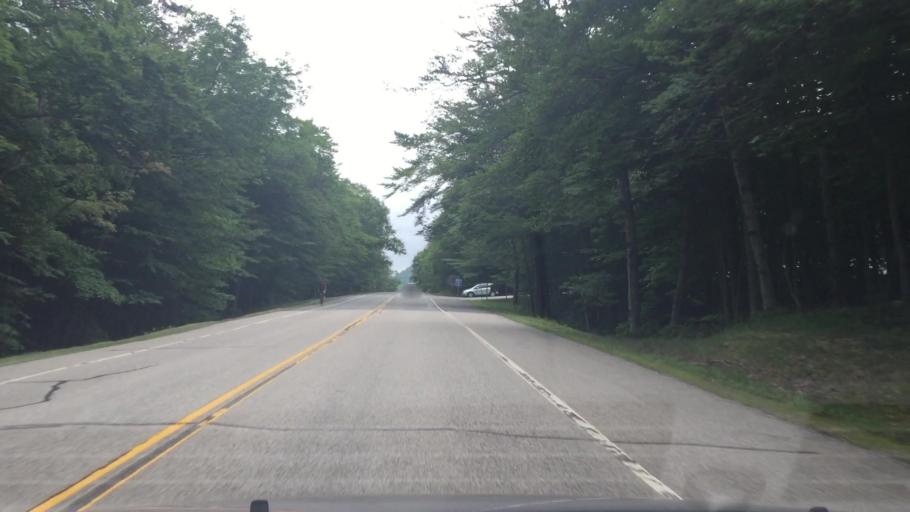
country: US
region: New Hampshire
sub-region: Carroll County
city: North Conway
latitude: 44.1490
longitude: -71.3661
